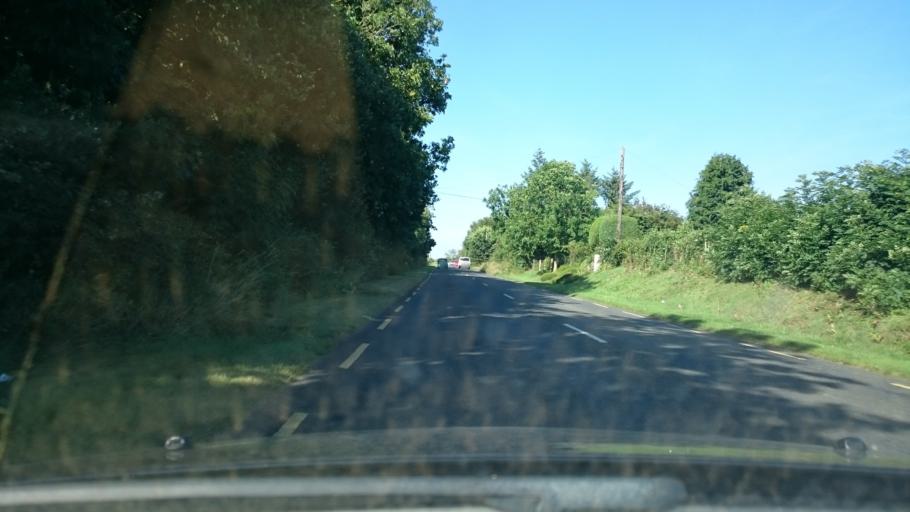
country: IE
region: Leinster
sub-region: Kilkenny
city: Graiguenamanagh
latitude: 52.5521
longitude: -6.9577
